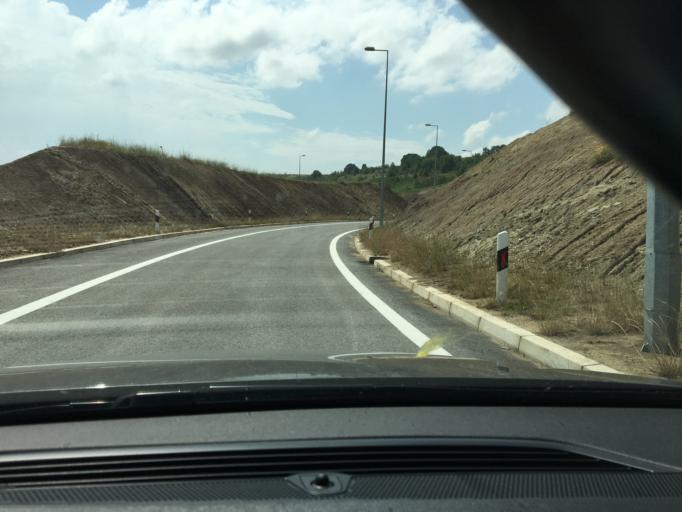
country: MK
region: Sveti Nikole
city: Gorobinci
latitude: 41.9174
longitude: 21.8763
